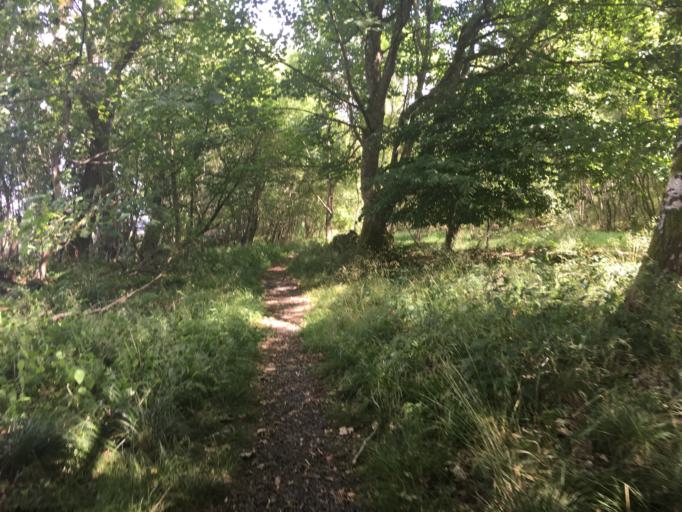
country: GB
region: Scotland
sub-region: Stirling
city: Stirling
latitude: 56.1065
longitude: -3.9804
